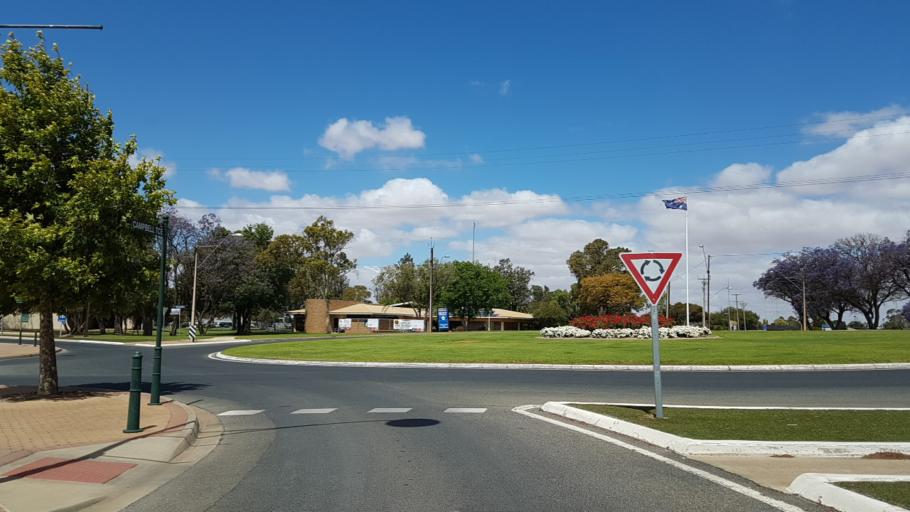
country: AU
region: South Australia
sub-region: Loxton Waikerie
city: Waikerie
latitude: -34.1815
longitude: 139.9856
